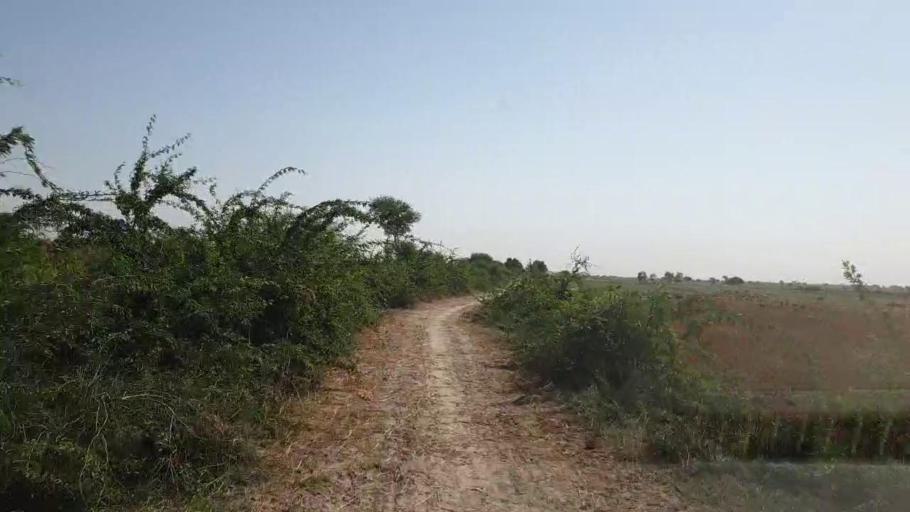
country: PK
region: Sindh
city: Kadhan
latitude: 24.6238
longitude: 68.9952
